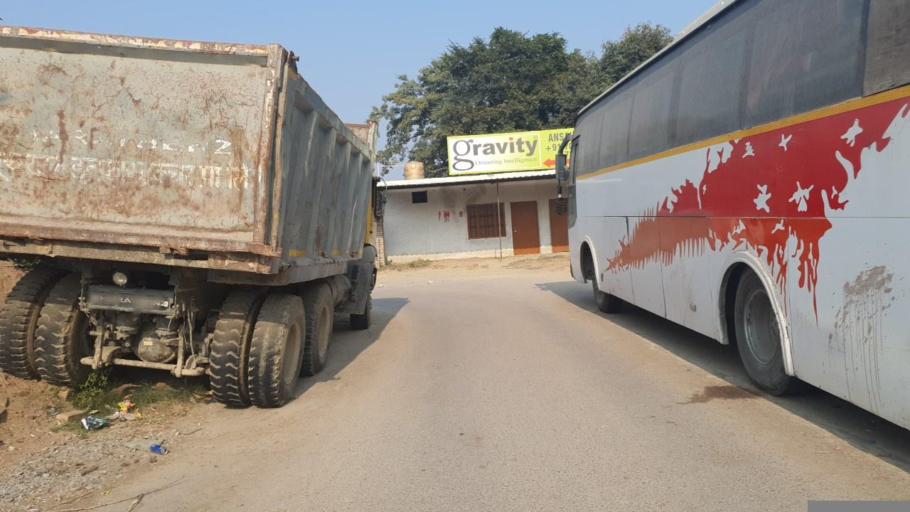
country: IN
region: Uttar Pradesh
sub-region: Lucknow District
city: Lucknow
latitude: 26.7945
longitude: 81.0098
